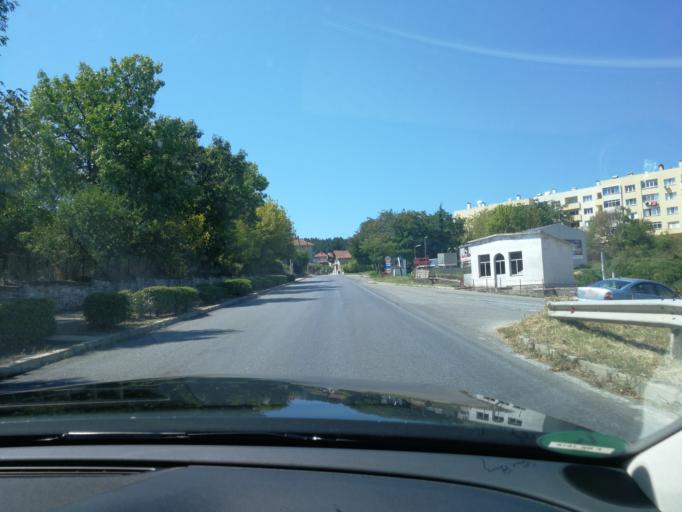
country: BG
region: Khaskovo
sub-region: Obshtina Topolovgrad
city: Topolovgrad
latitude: 42.0838
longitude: 26.3292
